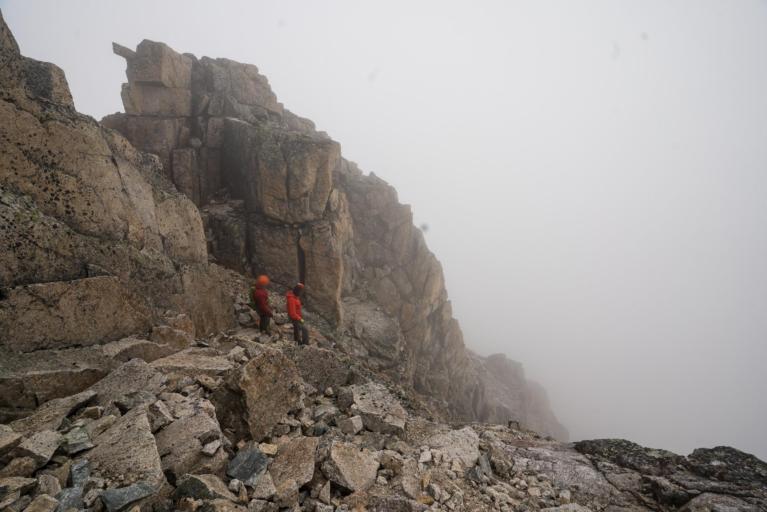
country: RU
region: Transbaikal Territory
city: Chara
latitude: 56.8656
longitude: 117.5797
